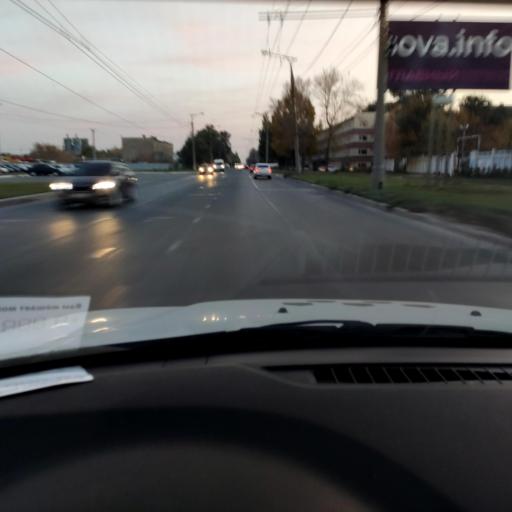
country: RU
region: Samara
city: Tol'yatti
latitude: 53.5606
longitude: 49.4541
